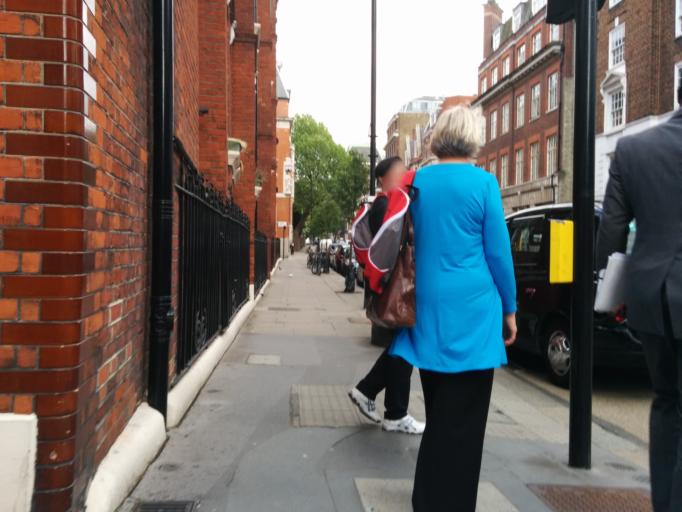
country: GB
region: England
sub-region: Greater London
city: London
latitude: 51.4970
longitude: -0.1293
